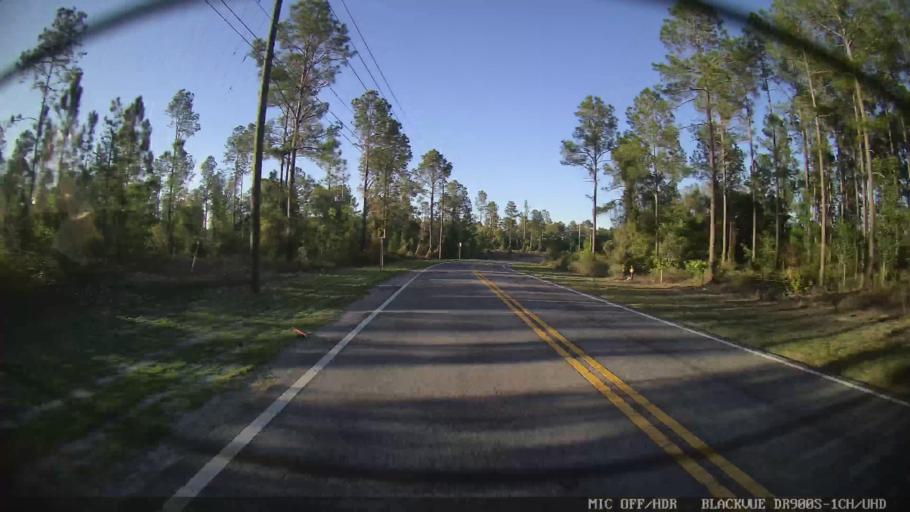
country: US
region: Florida
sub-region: Pasco County
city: Shady Hills
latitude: 28.3592
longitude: -82.5425
